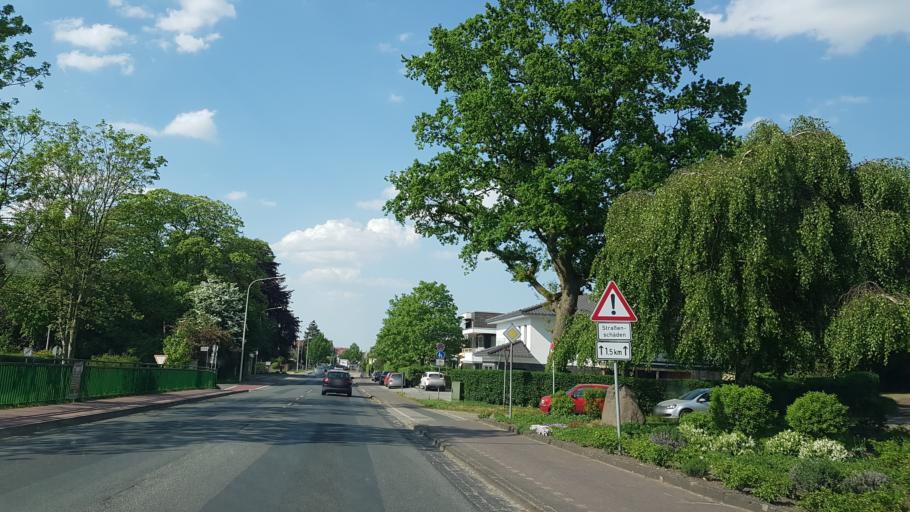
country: DE
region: Lower Saxony
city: Langen
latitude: 53.6006
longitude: 8.5954
